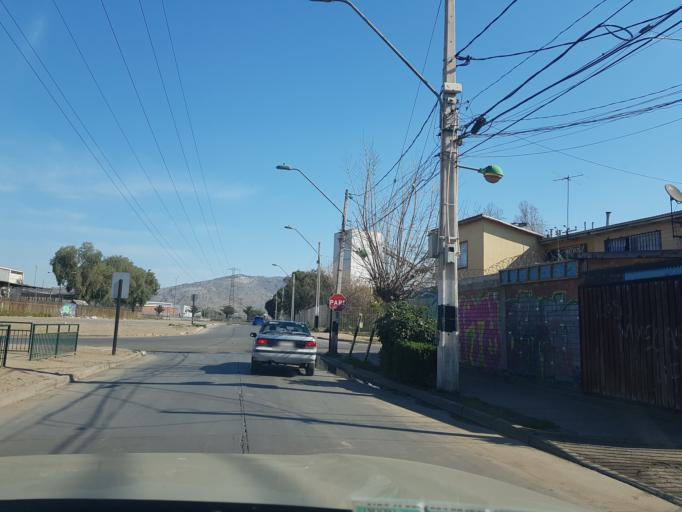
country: CL
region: Santiago Metropolitan
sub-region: Provincia de Santiago
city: Lo Prado
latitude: -33.3715
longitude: -70.7221
